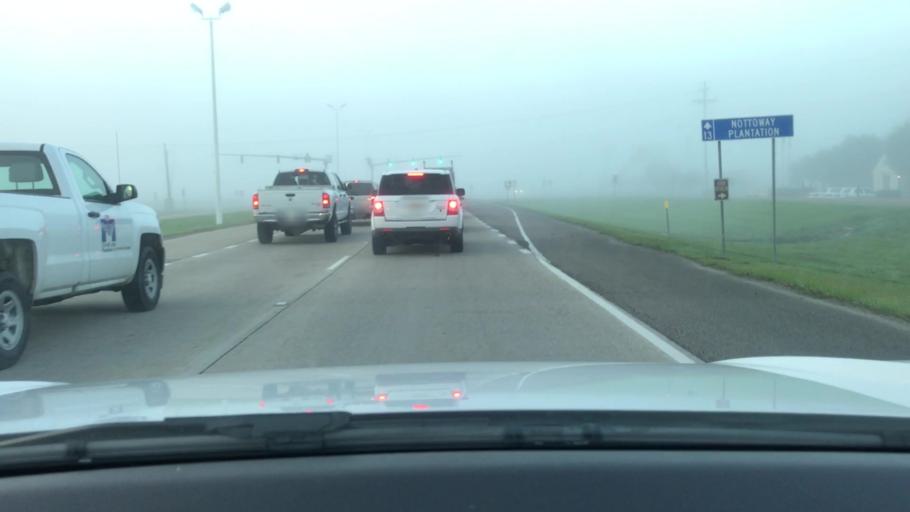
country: US
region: Louisiana
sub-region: West Baton Rouge Parish
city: Addis
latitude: 30.3567
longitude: -91.2599
